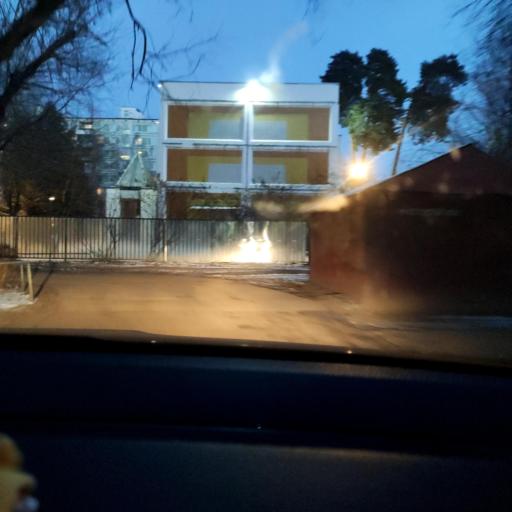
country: RU
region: Moscow
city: Vatutino
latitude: 55.8851
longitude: 37.6919
